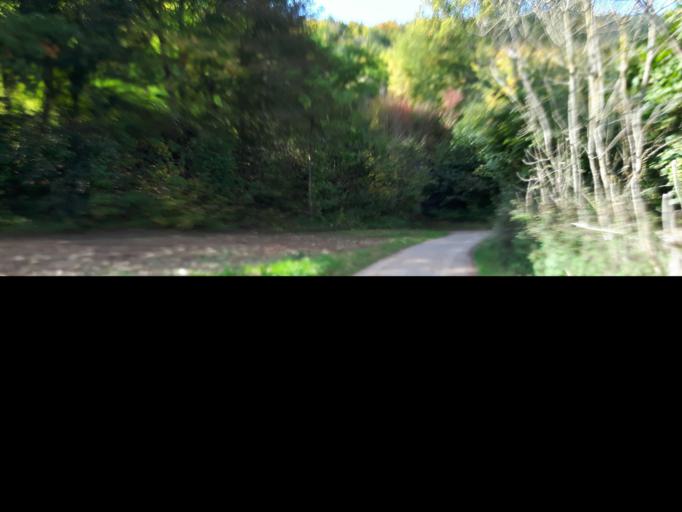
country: DE
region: Baden-Wuerttemberg
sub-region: Regierungsbezirk Stuttgart
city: Werbach
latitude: 49.6837
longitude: 9.6240
